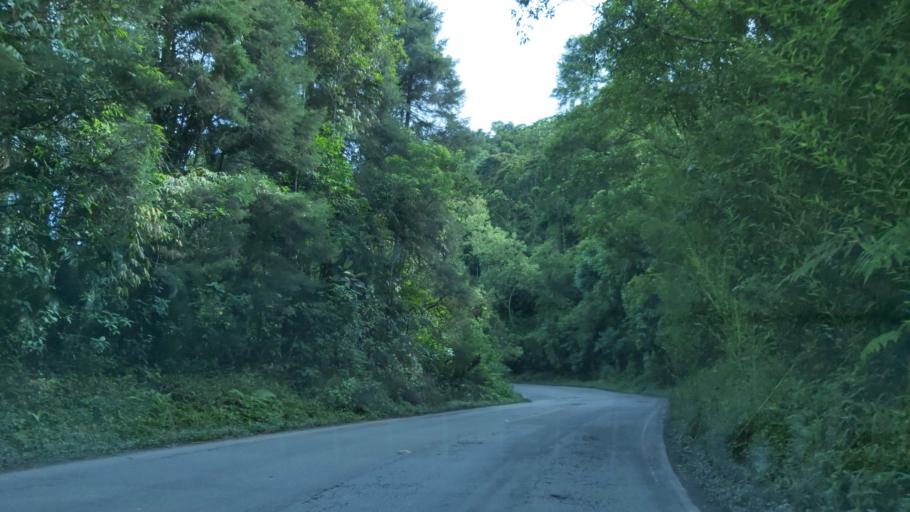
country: BR
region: Sao Paulo
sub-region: Miracatu
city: Miracatu
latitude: -24.0456
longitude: -47.5688
